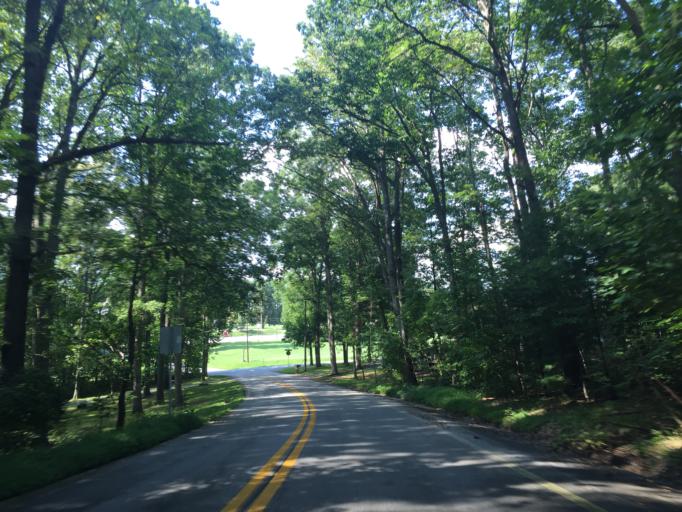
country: US
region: Maryland
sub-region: Carroll County
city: Manchester
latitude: 39.6408
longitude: -76.9159
